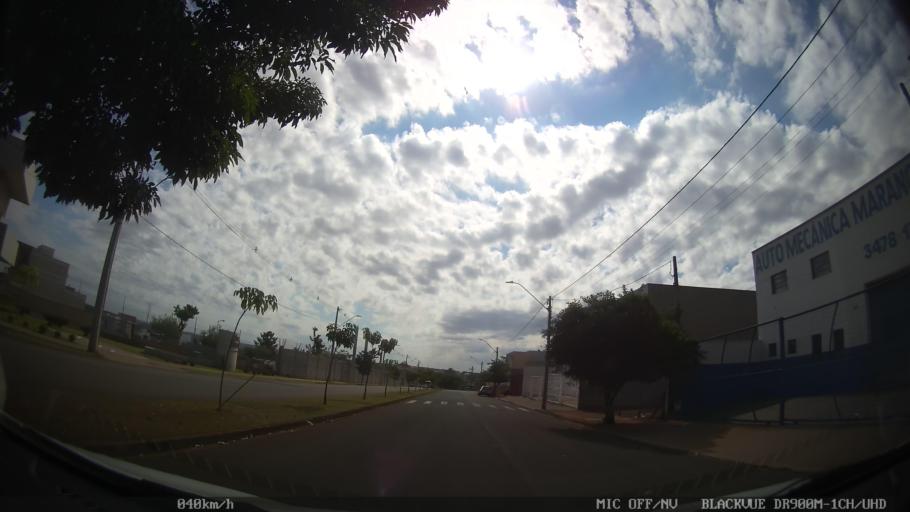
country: BR
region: Sao Paulo
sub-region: Americana
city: Americana
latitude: -22.7202
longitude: -47.3225
